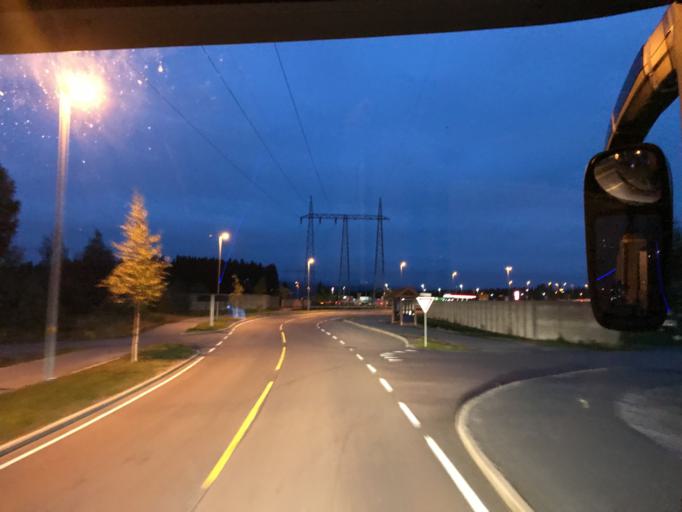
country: NO
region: Akershus
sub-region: Eidsvoll
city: Eidsvoll
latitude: 60.3929
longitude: 11.2107
